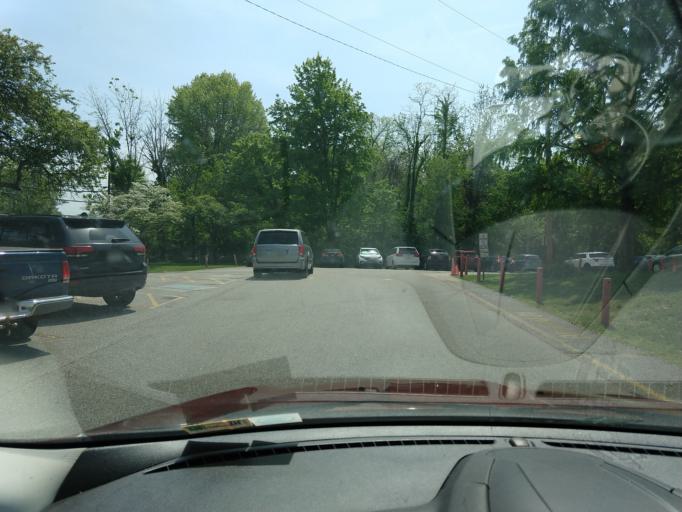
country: US
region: West Virginia
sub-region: Kanawha County
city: Saint Albans
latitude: 38.3832
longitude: -81.8310
